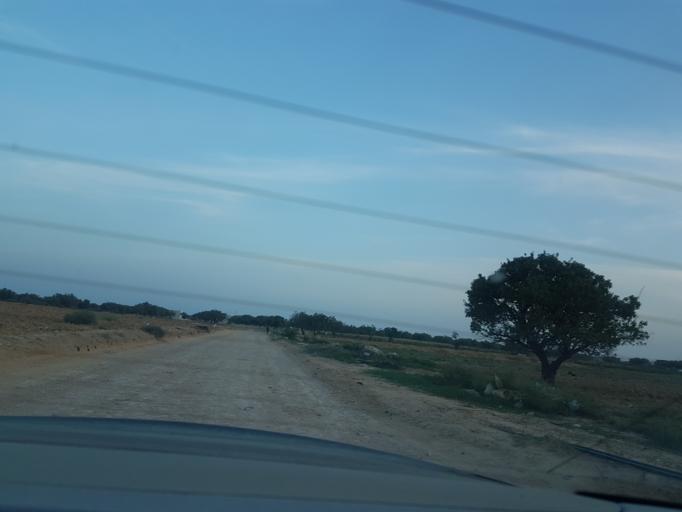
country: TN
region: Safaqis
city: Sfax
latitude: 34.7064
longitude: 10.6908
